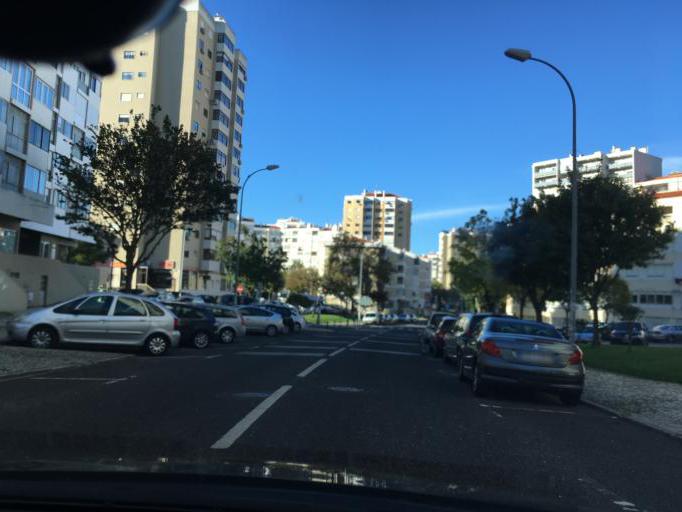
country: PT
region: Lisbon
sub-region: Odivelas
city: Pontinha
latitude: 38.7616
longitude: -9.2069
